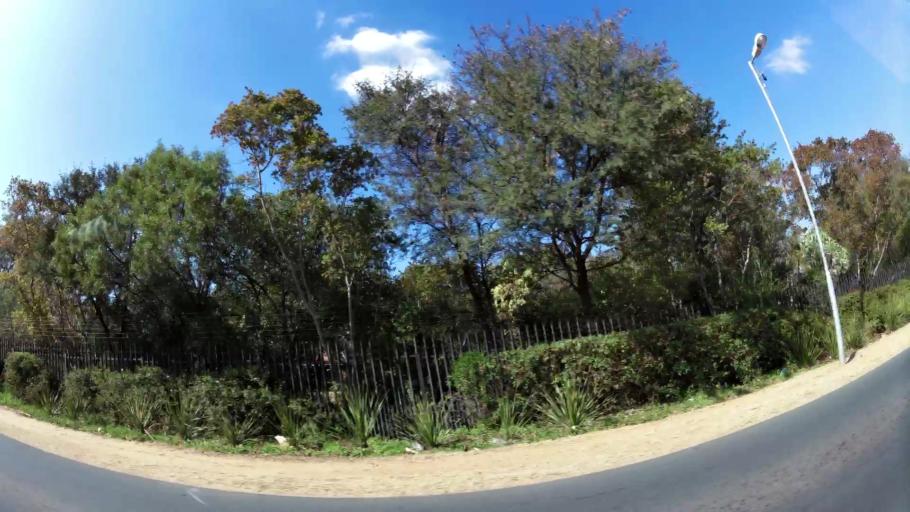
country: ZA
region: Gauteng
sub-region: West Rand District Municipality
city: Muldersdriseloop
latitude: -26.0483
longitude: 27.9296
